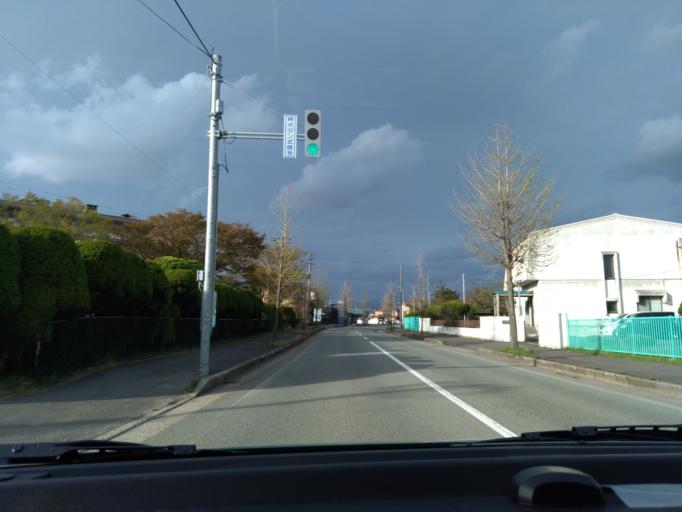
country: JP
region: Akita
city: Akita Shi
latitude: 39.7568
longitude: 140.0769
